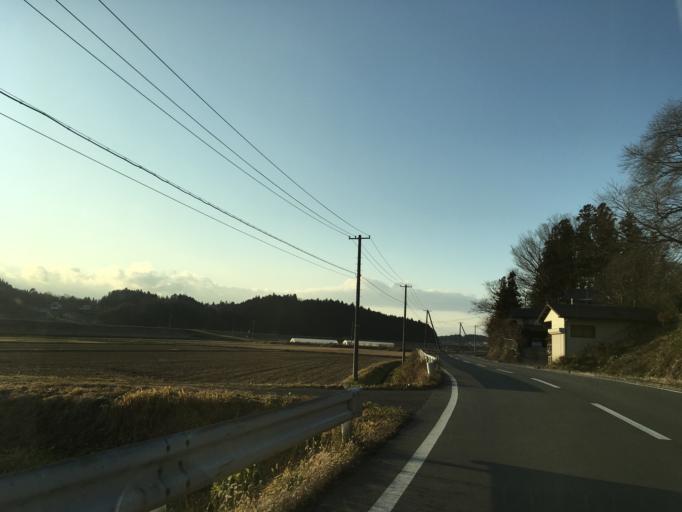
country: JP
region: Iwate
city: Ichinoseki
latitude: 38.8081
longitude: 141.2178
